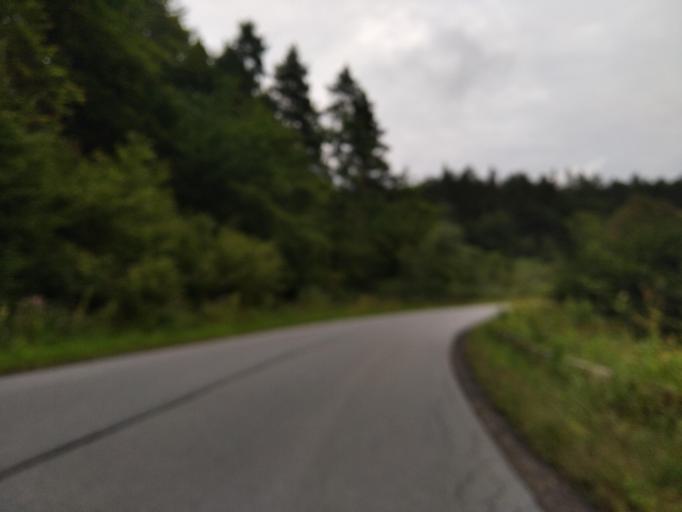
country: PL
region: Subcarpathian Voivodeship
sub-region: Powiat przemyski
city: Bircza
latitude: 49.6886
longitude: 22.4142
